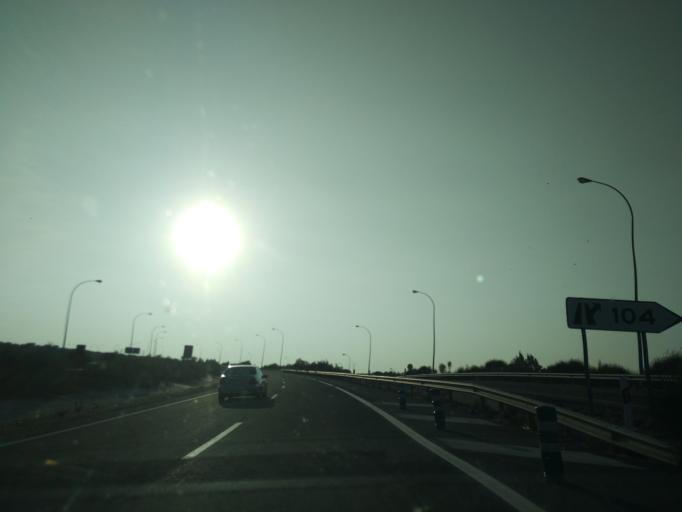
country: ES
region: Castille and Leon
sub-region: Provincia de Avila
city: Berrocalejo de Aragona
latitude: 40.6784
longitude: -4.6309
